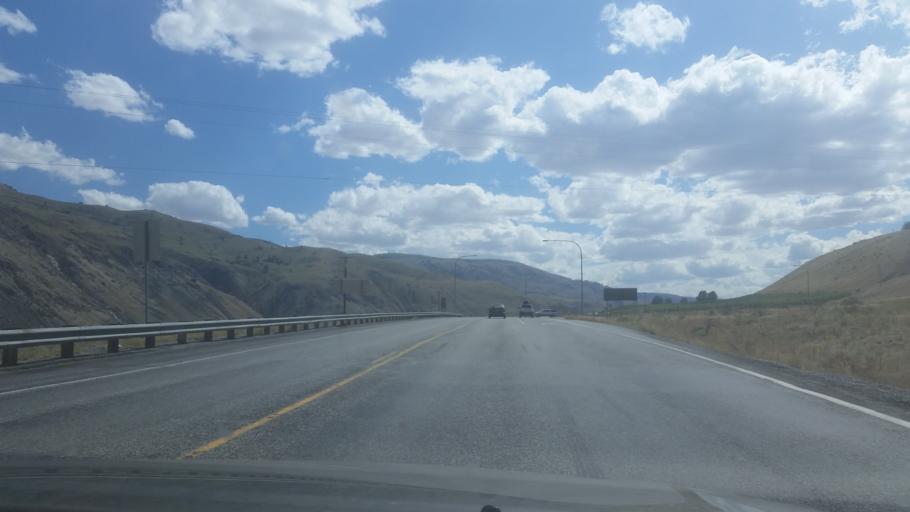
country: US
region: Washington
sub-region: Chelan County
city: Chelan
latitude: 47.8742
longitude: -119.9199
